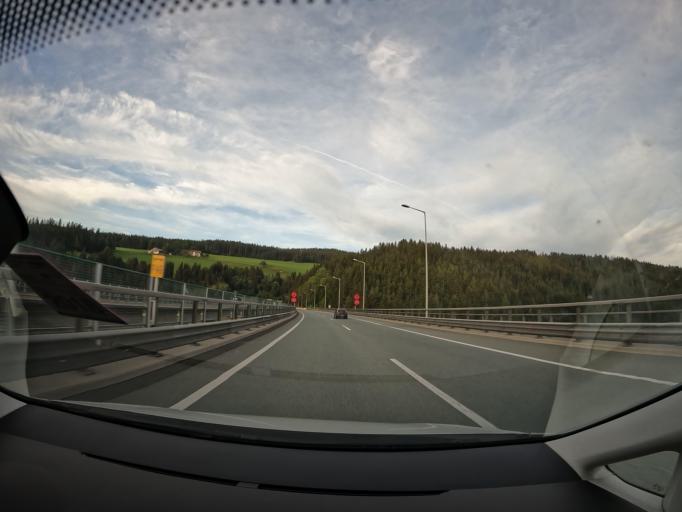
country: AT
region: Styria
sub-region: Politischer Bezirk Voitsberg
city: Pack
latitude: 46.9378
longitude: 15.0009
